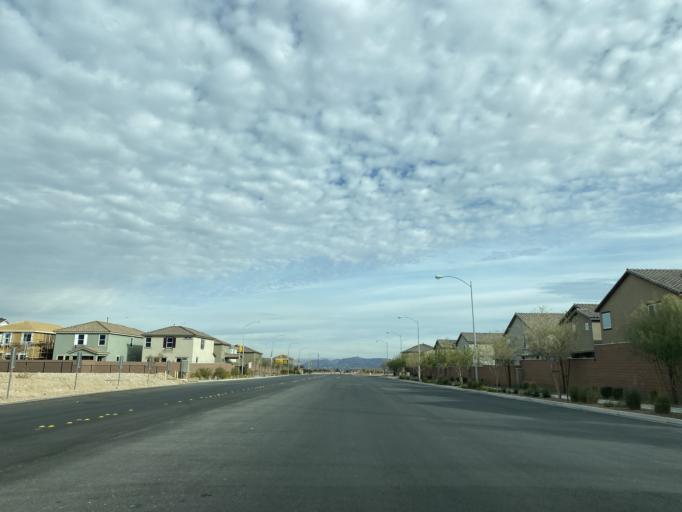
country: US
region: Nevada
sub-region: Clark County
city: Enterprise
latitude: 35.9979
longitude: -115.2761
